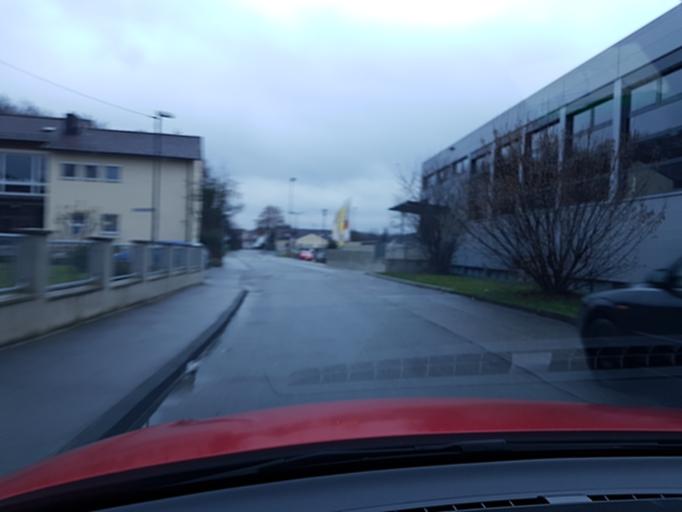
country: DE
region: Baden-Wuerttemberg
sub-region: Karlsruhe Region
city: Muhlacker
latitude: 48.9773
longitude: 8.8636
